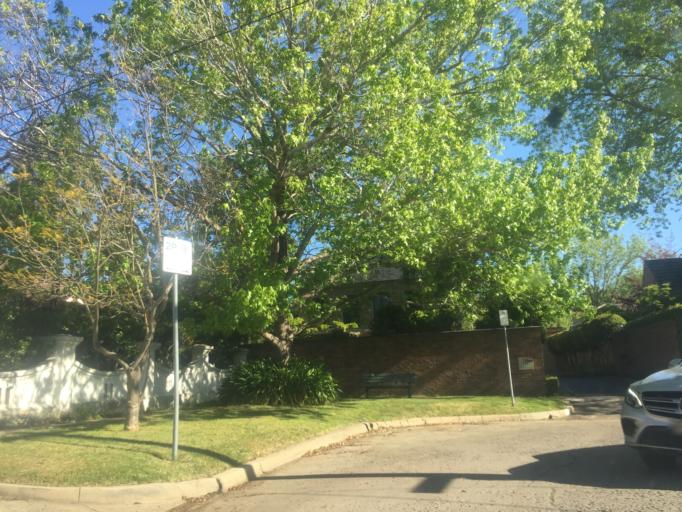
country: AU
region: Victoria
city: Balwyn
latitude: -37.8144
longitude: 145.0721
